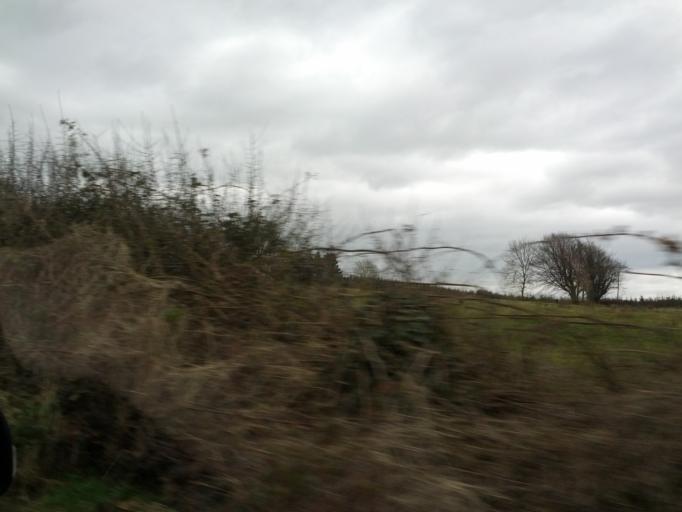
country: IE
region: Connaught
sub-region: County Galway
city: Athenry
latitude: 53.3877
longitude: -8.6369
